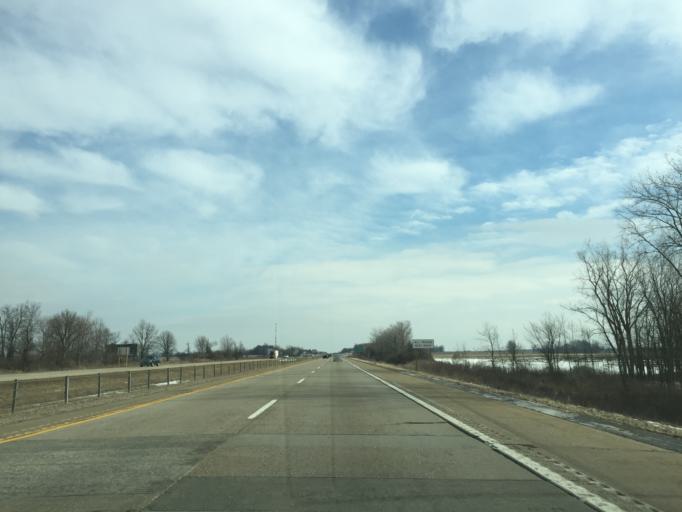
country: US
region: Michigan
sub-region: Ionia County
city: Ionia
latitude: 42.8790
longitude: -85.0543
